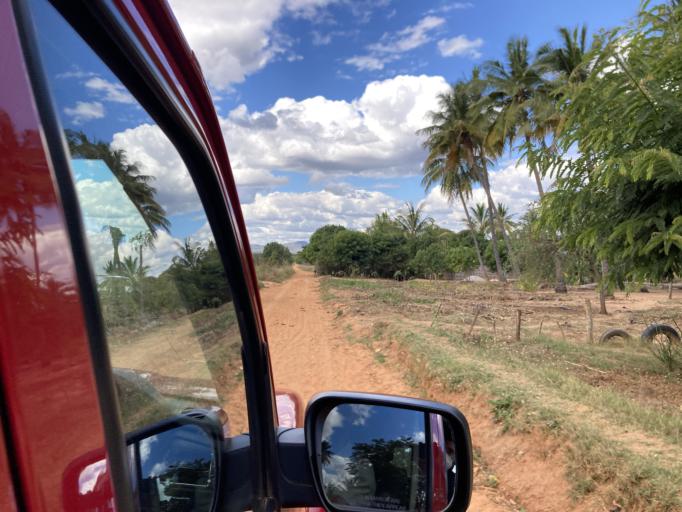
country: MZ
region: Cabo Delgado
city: Montepuez
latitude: -13.1265
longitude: 39.0373
